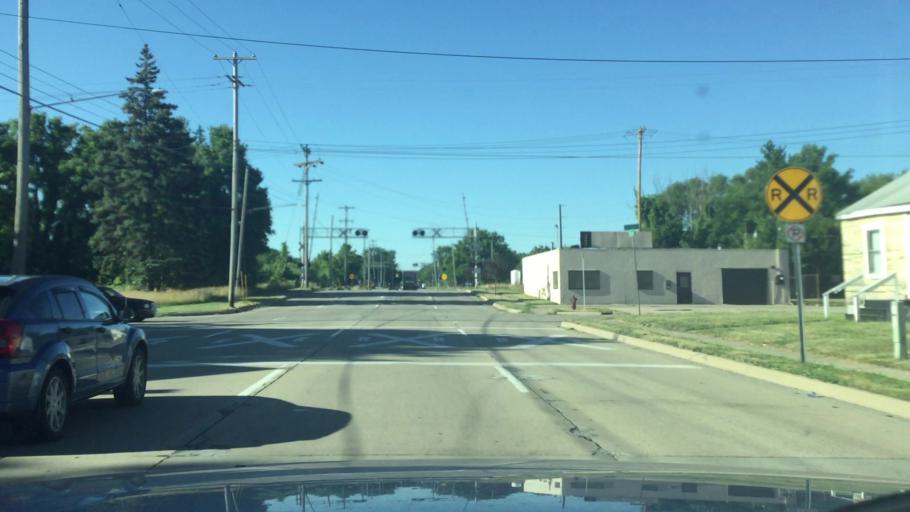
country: US
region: Michigan
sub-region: Saginaw County
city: Saginaw
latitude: 43.4133
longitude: -83.9360
